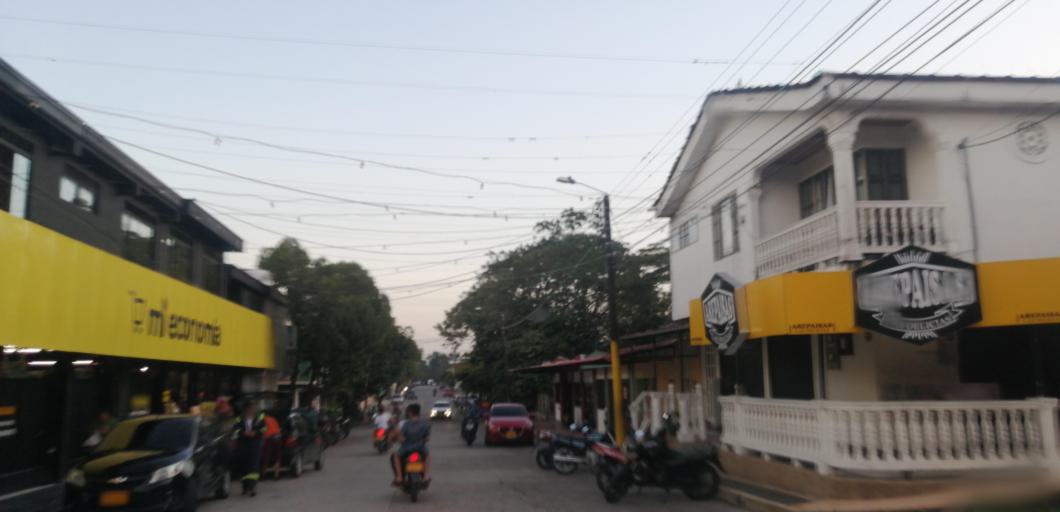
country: CO
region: Meta
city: Acacias
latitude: 3.9931
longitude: -73.7582
